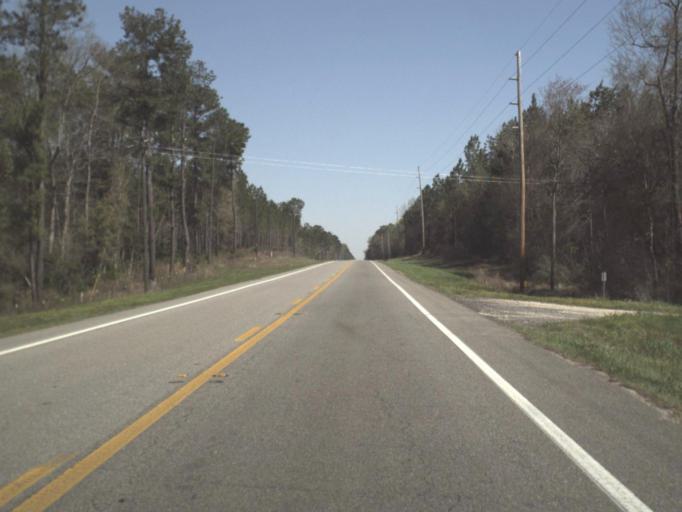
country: US
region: Florida
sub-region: Liberty County
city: Bristol
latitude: 30.3882
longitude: -84.7833
